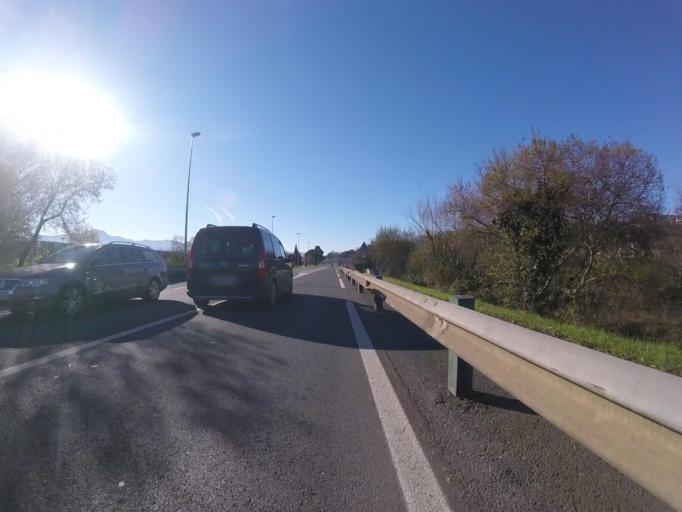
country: ES
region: Basque Country
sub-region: Provincia de Guipuzcoa
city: Fuenterrabia
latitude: 43.3580
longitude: -1.7932
